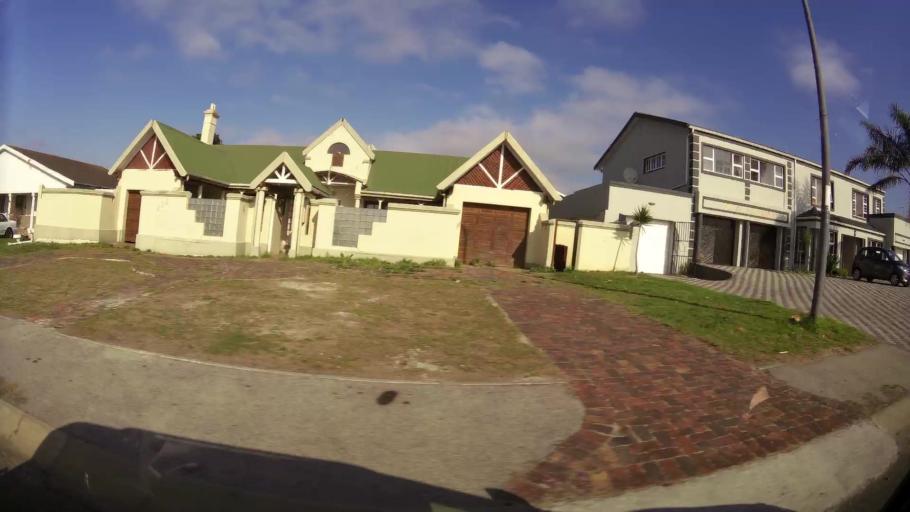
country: ZA
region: Eastern Cape
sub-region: Nelson Mandela Bay Metropolitan Municipality
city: Port Elizabeth
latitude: -33.9208
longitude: 25.5313
